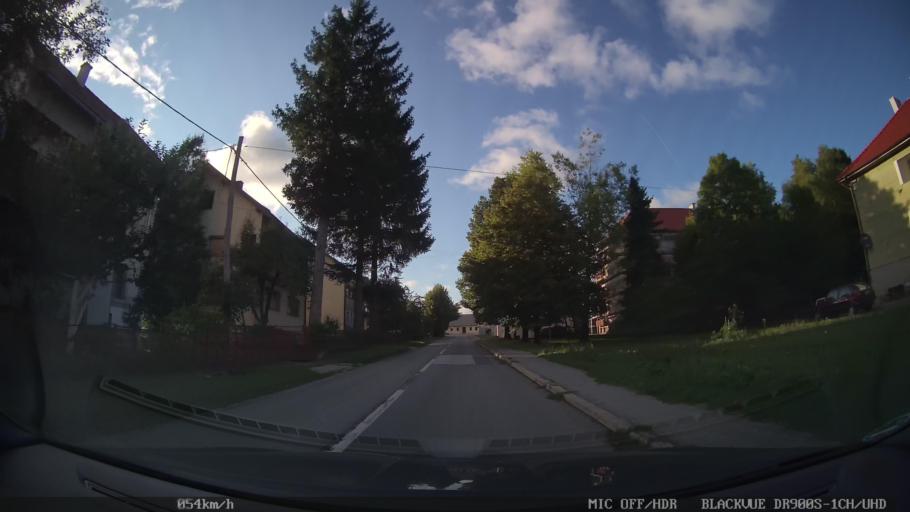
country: HR
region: Karlovacka
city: Plaski
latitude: 45.0799
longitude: 15.3623
